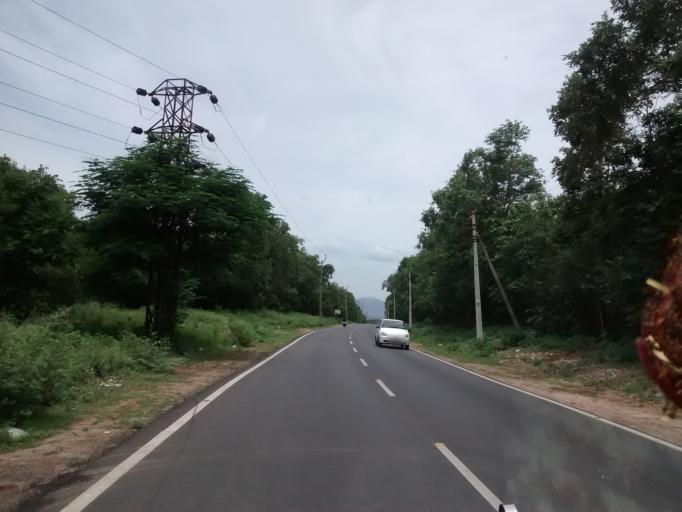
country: IN
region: Andhra Pradesh
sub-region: Chittoor
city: Tirupati
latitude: 13.6409
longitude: 79.3979
